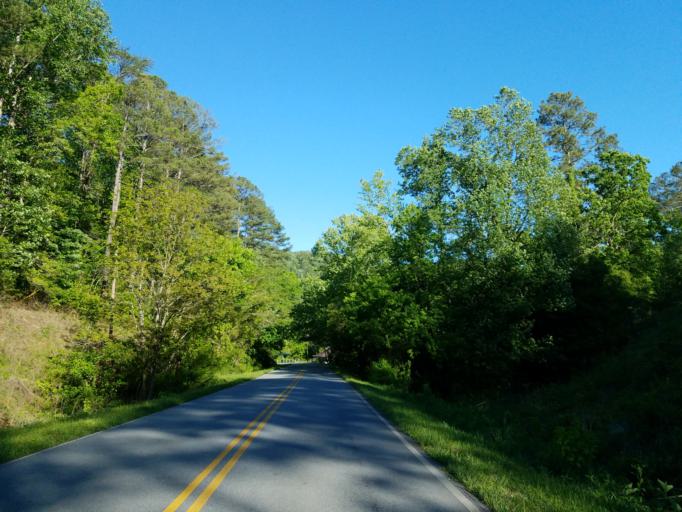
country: US
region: Georgia
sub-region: Pickens County
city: Jasper
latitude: 34.5663
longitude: -84.5138
